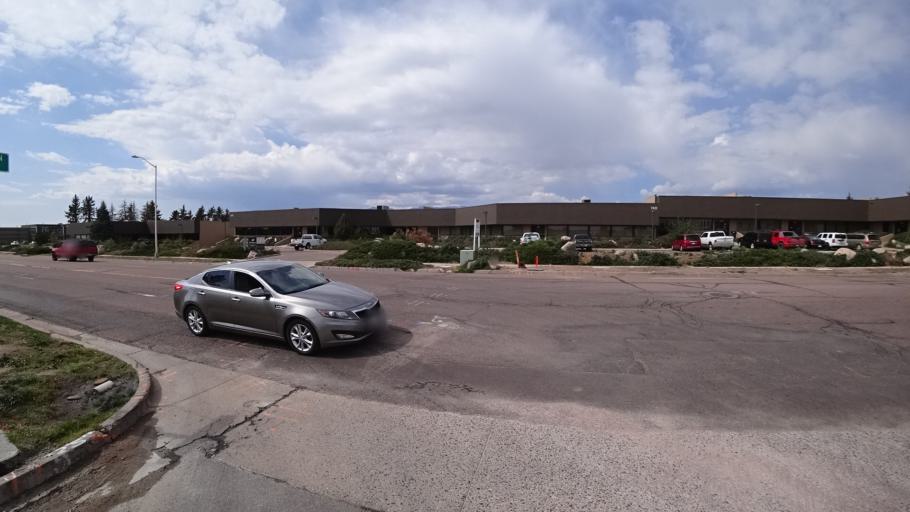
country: US
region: Colorado
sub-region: El Paso County
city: Cimarron Hills
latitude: 38.8441
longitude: -104.7386
